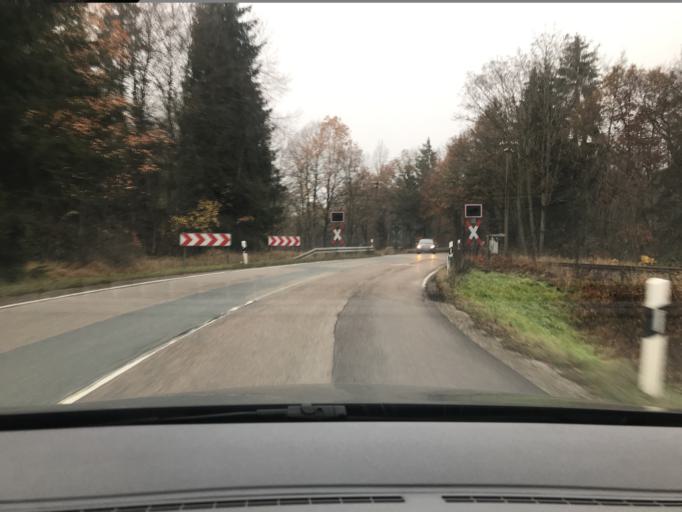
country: DE
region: Bavaria
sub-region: Regierungsbezirk Mittelfranken
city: Wilburgstetten
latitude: 48.9941
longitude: 10.4179
